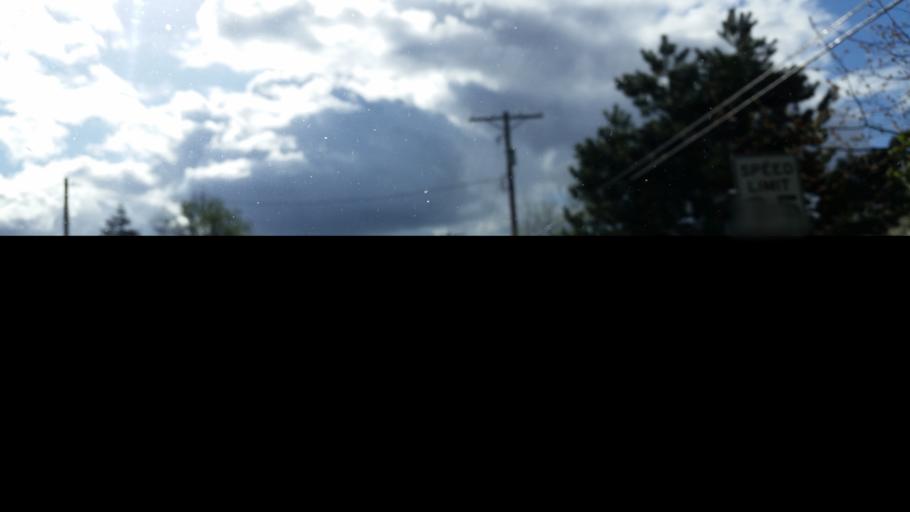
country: US
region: Washington
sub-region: Pierce County
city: Graham
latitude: 47.0529
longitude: -122.2844
